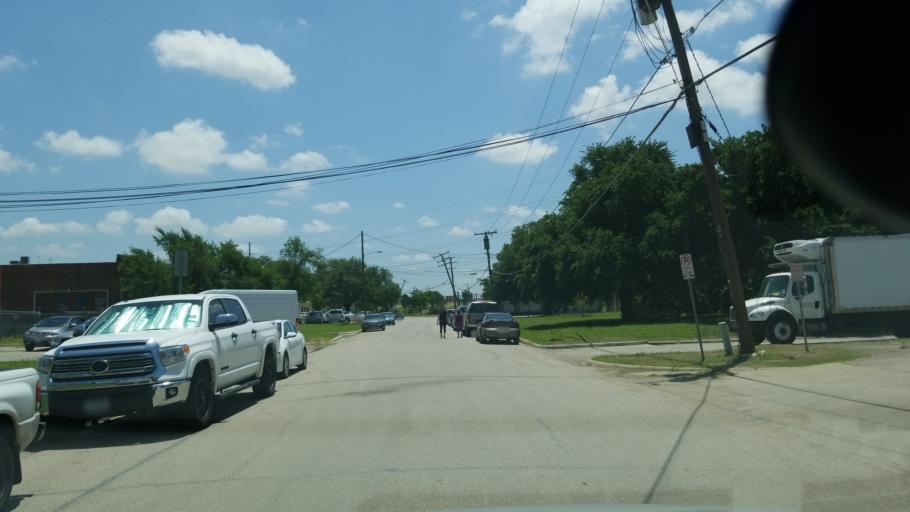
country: US
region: Texas
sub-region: Dallas County
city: Irving
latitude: 32.8149
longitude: -96.8786
